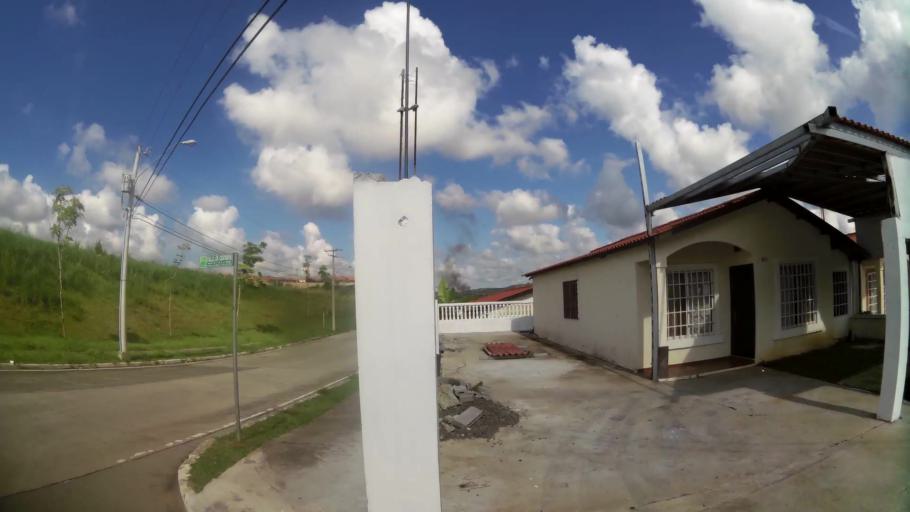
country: PA
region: Panama
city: Nuevo Arraijan
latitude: 8.9028
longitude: -79.7407
